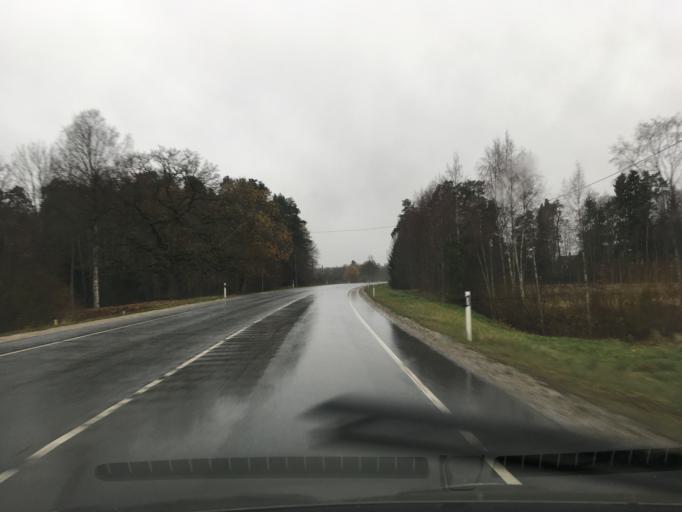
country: EE
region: Harju
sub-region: Nissi vald
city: Turba
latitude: 58.8996
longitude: 24.1075
